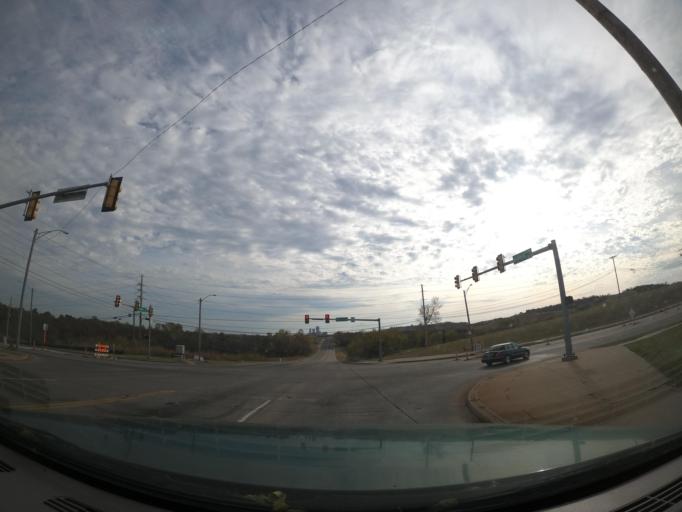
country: US
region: Oklahoma
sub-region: Tulsa County
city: Turley
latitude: 36.2062
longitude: -95.9936
